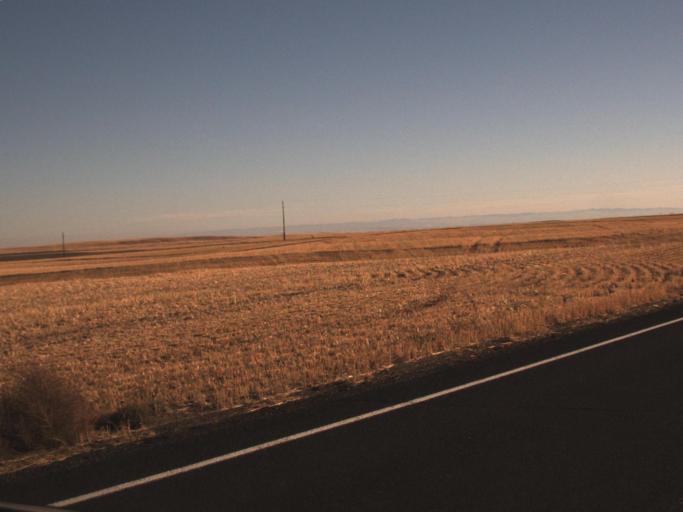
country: US
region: Washington
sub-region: Adams County
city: Ritzville
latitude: 46.8705
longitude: -118.3357
